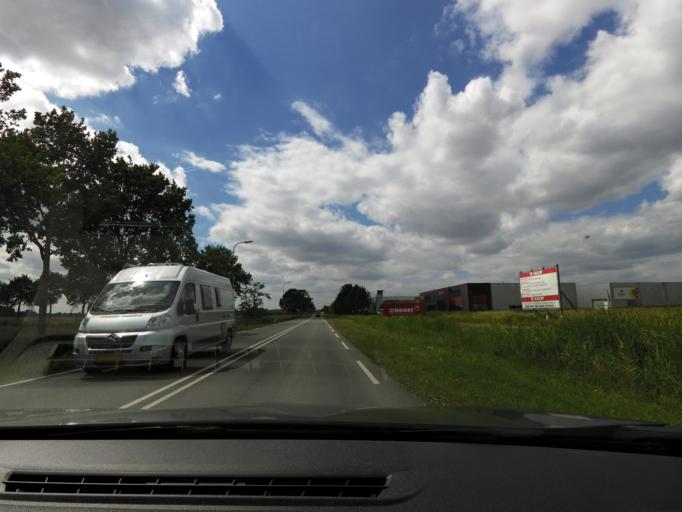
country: NL
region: North Brabant
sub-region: Gemeente Dongen
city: Dongen
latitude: 51.6130
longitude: 4.9341
